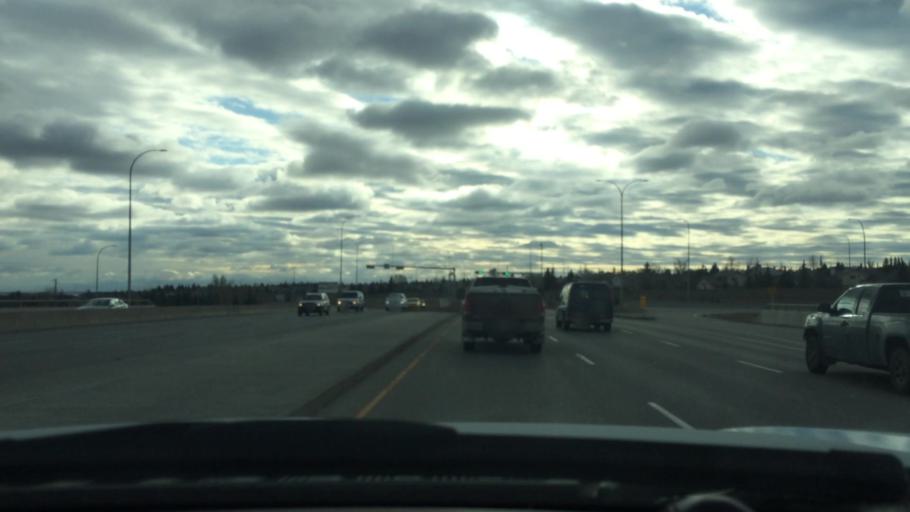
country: CA
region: Alberta
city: Calgary
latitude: 51.1441
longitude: -114.0928
